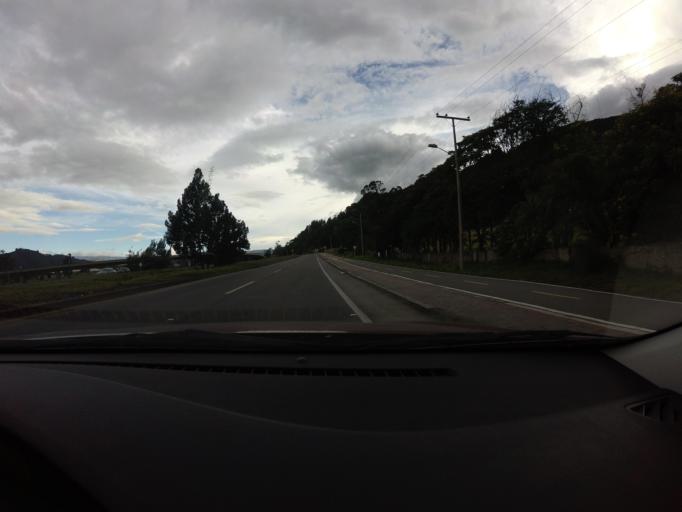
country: CO
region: Cundinamarca
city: Zipaquira
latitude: 4.9972
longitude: -74.0037
